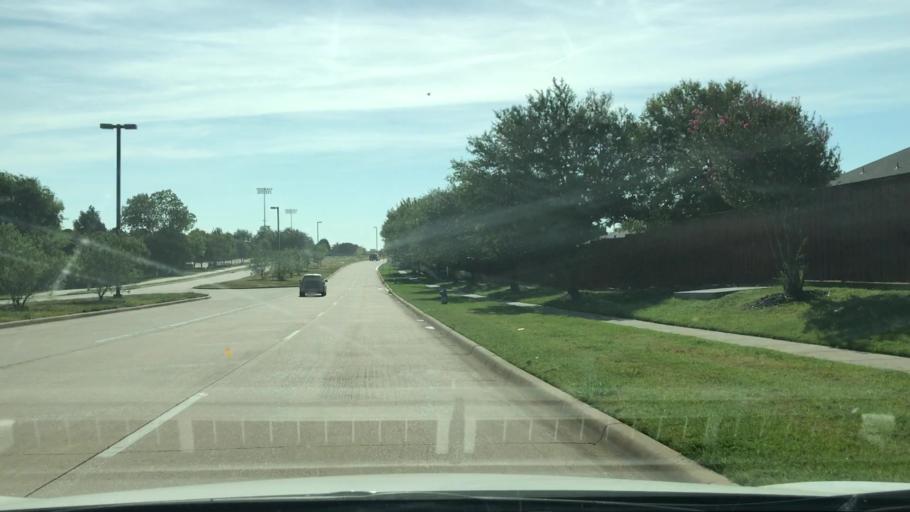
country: US
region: Texas
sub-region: Collin County
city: McKinney
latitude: 33.2320
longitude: -96.6488
